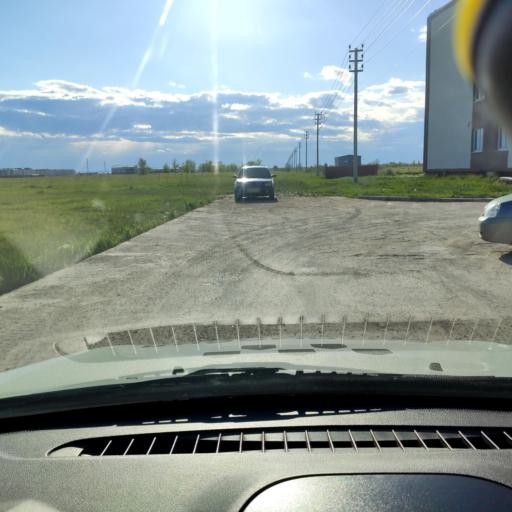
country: RU
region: Samara
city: Podstepki
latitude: 53.5321
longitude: 49.1970
